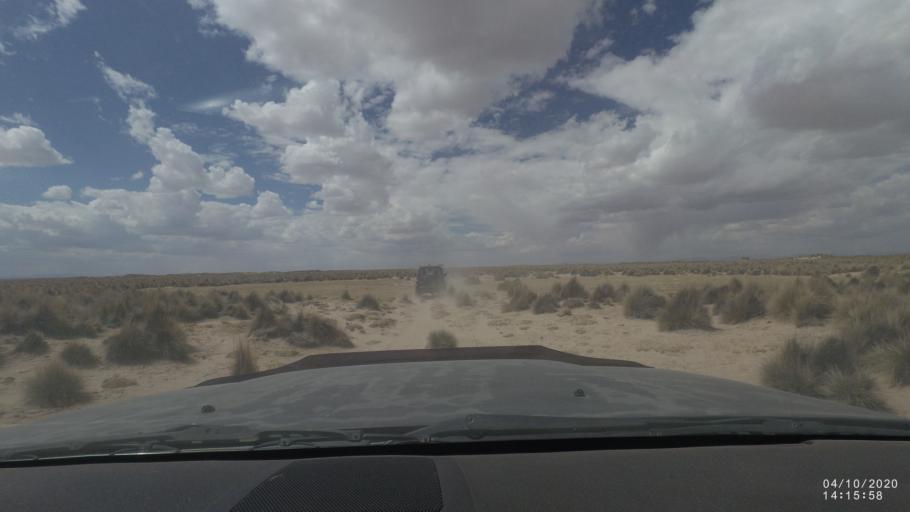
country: BO
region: Oruro
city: Poopo
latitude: -18.6916
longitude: -67.4532
